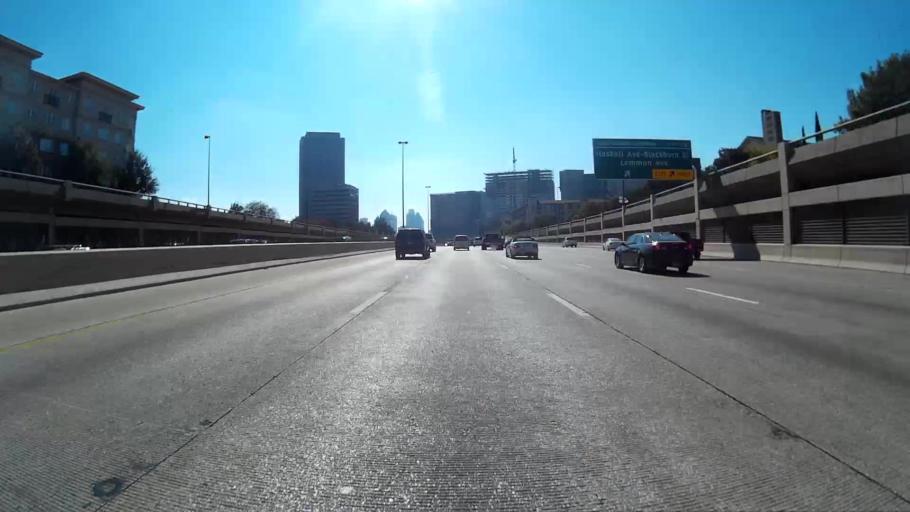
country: US
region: Texas
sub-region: Dallas County
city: Highland Park
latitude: 32.8120
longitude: -96.7914
